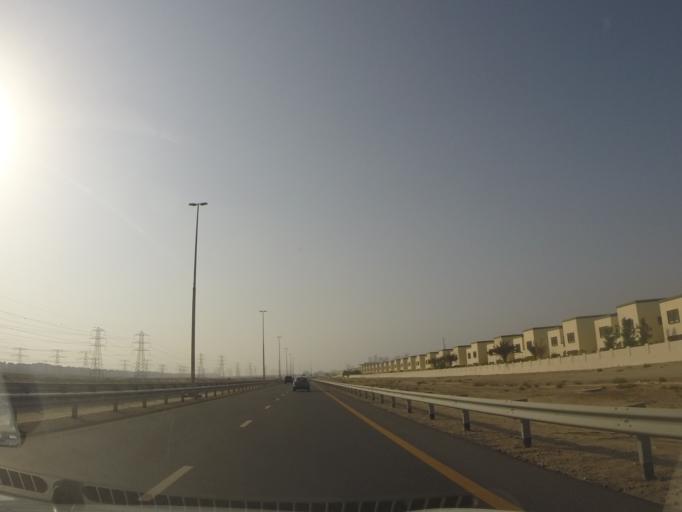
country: AE
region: Dubai
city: Dubai
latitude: 25.0387
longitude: 55.1590
